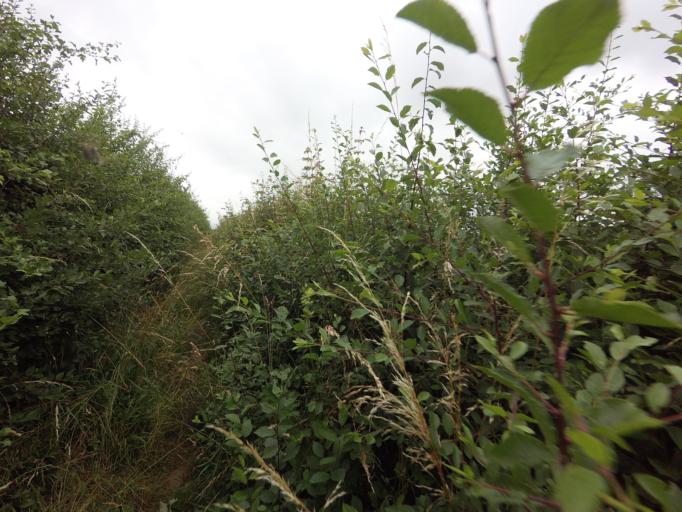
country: NL
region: Limburg
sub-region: Gemeente Maastricht
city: Heer
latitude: 50.8156
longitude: 5.7708
